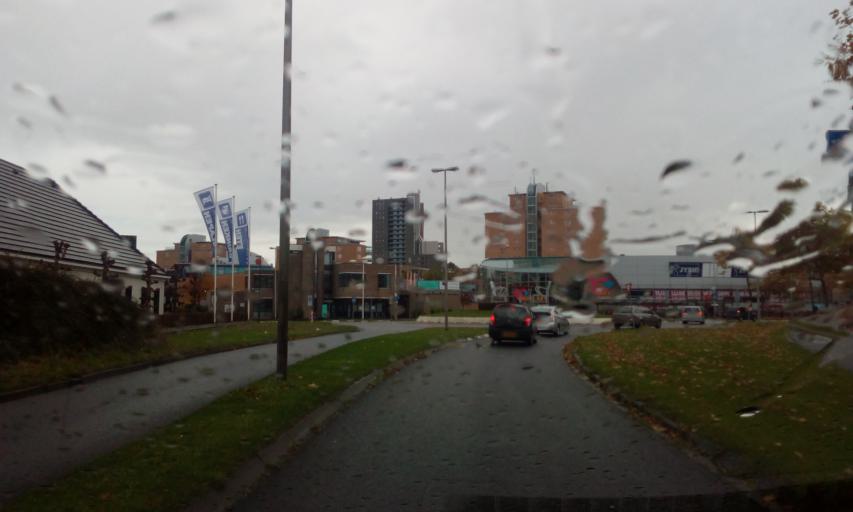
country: NL
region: South Holland
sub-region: Gemeente Zoetermeer
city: Zoetermeer
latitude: 52.0659
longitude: 4.4898
